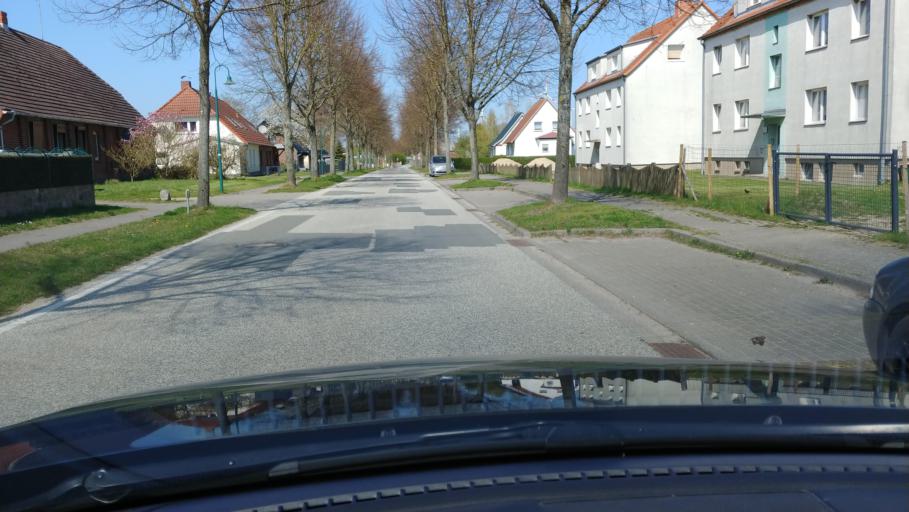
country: DE
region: Mecklenburg-Vorpommern
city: Muhlen Eichsen
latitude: 53.7800
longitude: 11.2648
